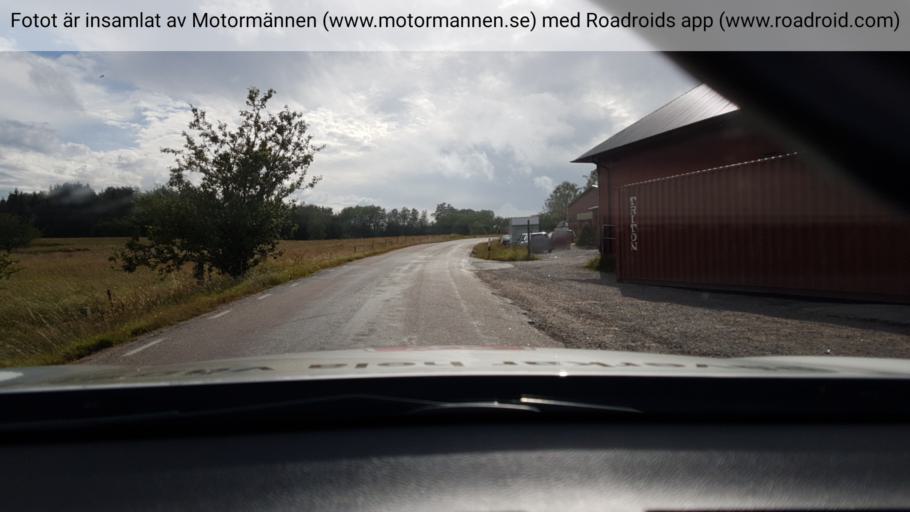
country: SE
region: Vaestra Goetaland
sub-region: Orust
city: Henan
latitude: 58.1627
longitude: 11.6965
